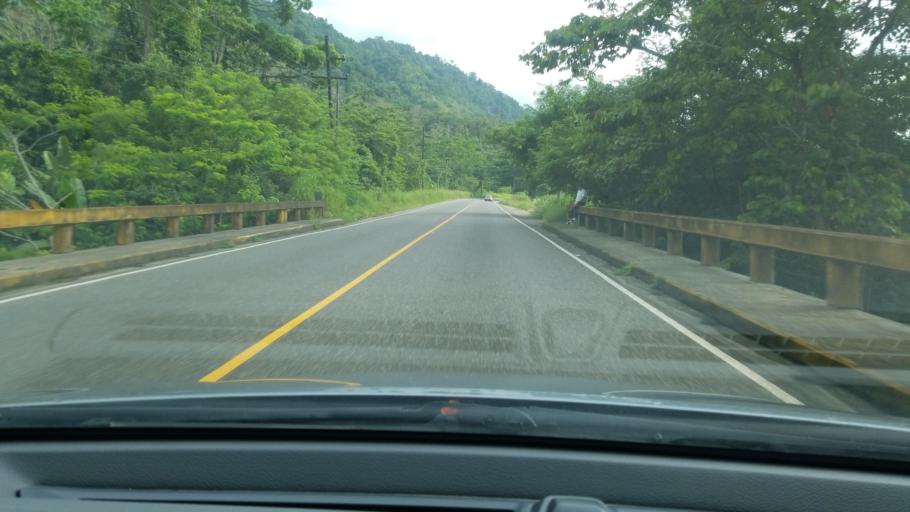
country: HN
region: Cortes
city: Potrerillos
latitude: 15.5980
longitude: -88.2990
